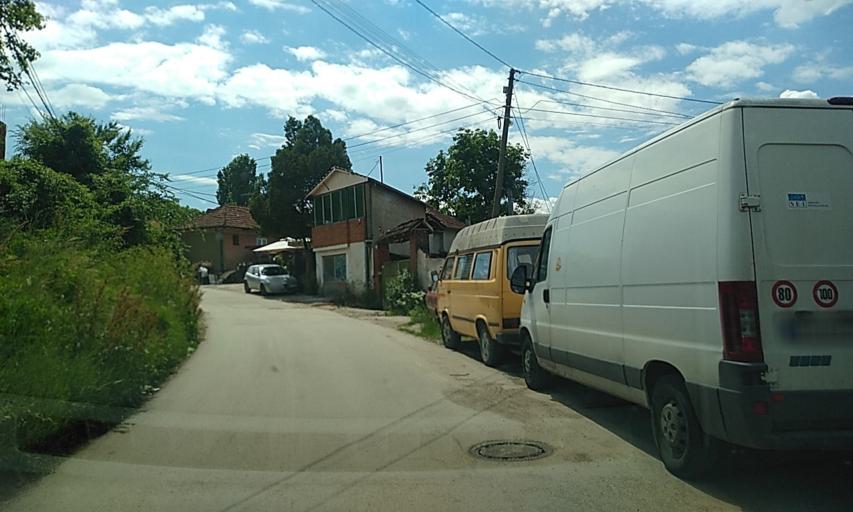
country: RS
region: Central Serbia
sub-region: Nisavski Okrug
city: Niska Banja
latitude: 43.2971
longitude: 22.0141
